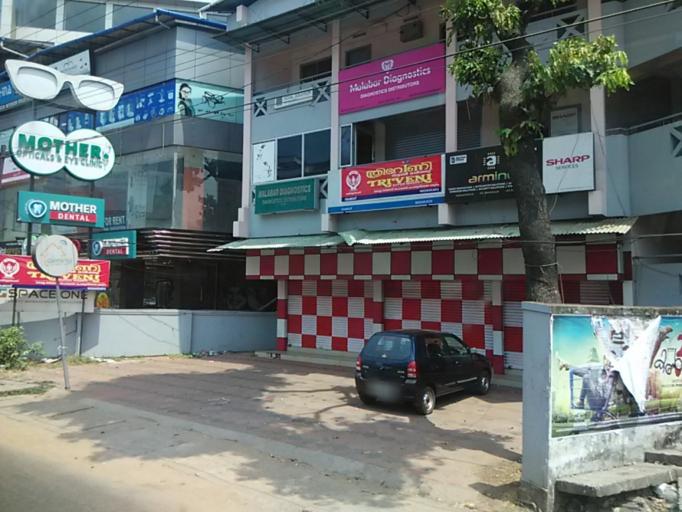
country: IN
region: Kerala
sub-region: Kozhikode
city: Kozhikode
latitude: 11.2737
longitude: 75.7746
